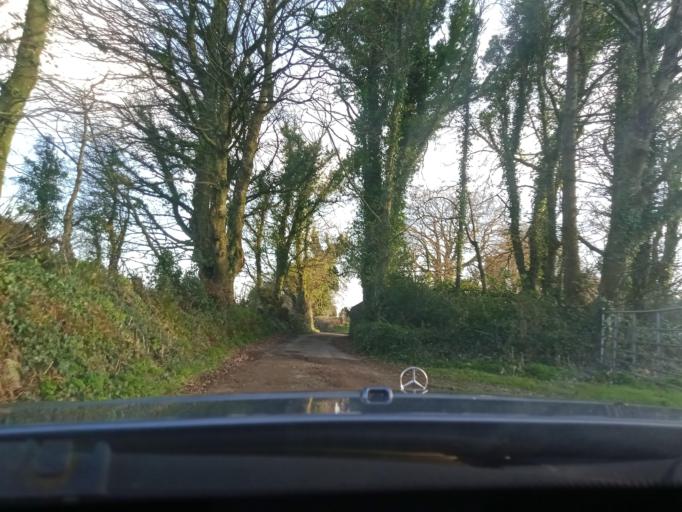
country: IE
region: Leinster
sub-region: Kilkenny
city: Callan
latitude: 52.4737
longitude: -7.4363
